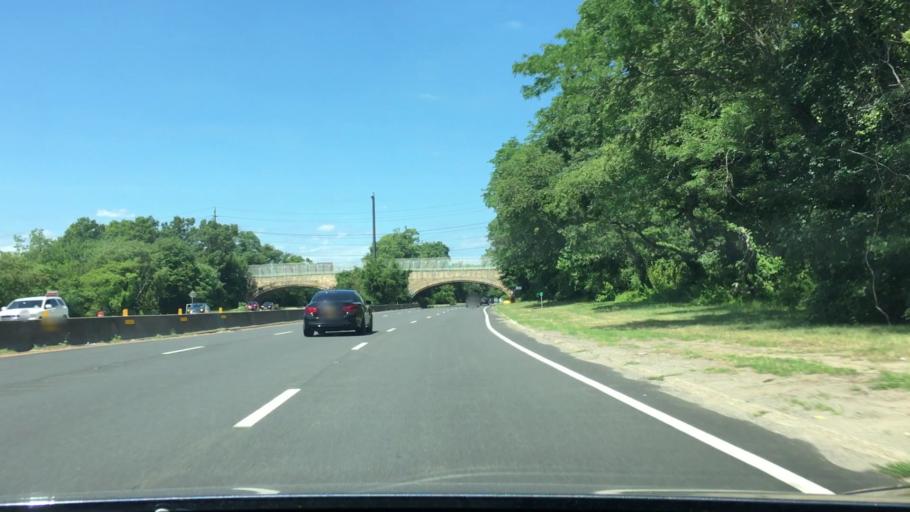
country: US
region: New York
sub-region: Nassau County
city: Wantagh
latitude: 40.6729
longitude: -73.5139
